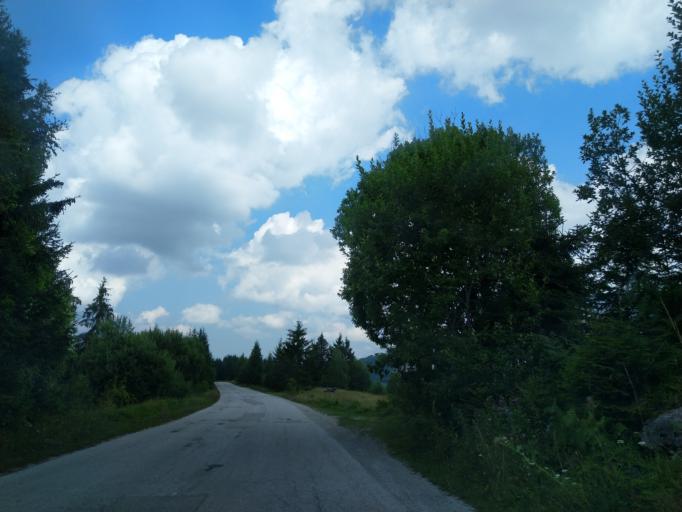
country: RS
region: Central Serbia
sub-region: Zlatiborski Okrug
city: Nova Varos
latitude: 43.5294
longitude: 19.8895
